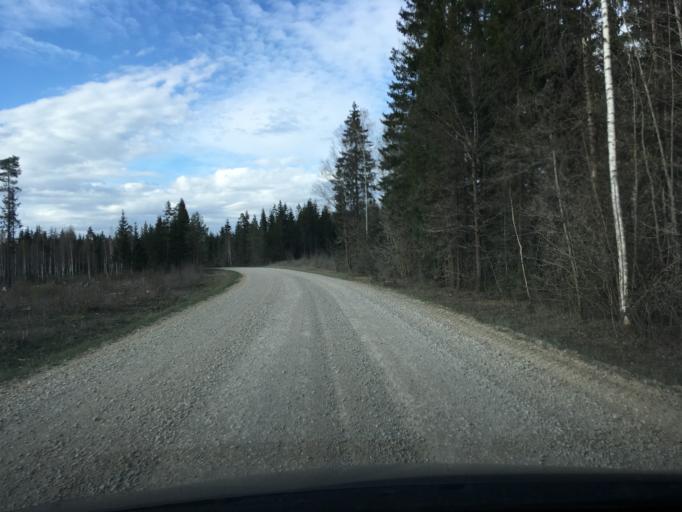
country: EE
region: Raplamaa
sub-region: Maerjamaa vald
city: Marjamaa
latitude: 58.9607
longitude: 24.3293
